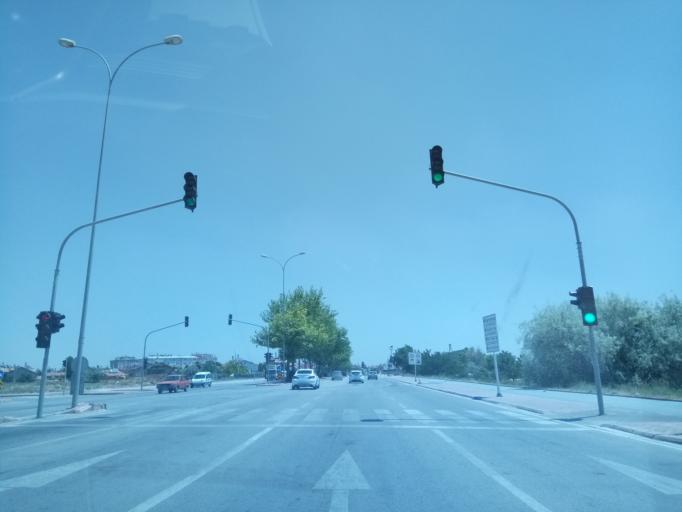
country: TR
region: Konya
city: Meram
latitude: 37.8285
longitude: 32.4771
